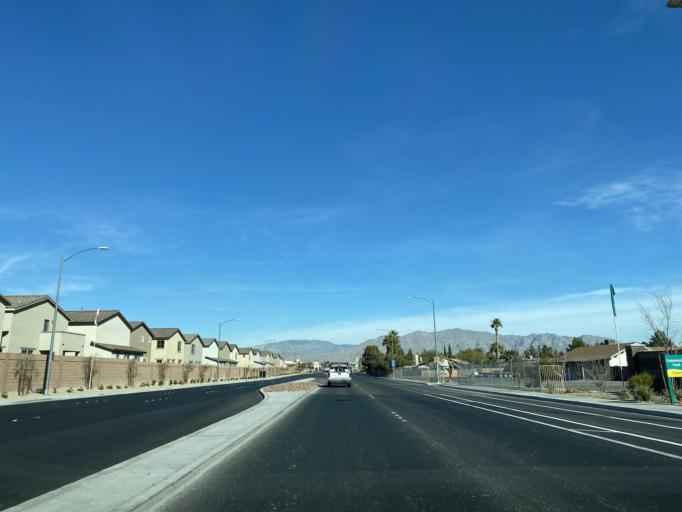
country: US
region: Nevada
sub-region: Clark County
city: Las Vegas
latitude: 36.2351
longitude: -115.2254
